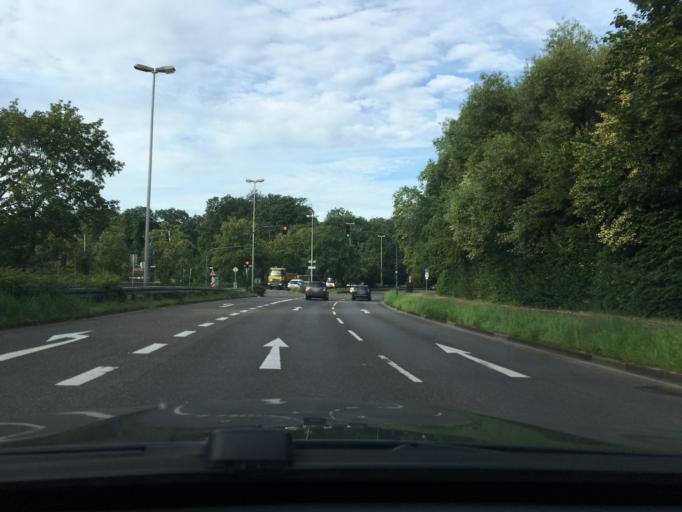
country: DE
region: North Rhine-Westphalia
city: Opladen
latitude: 51.0367
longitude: 7.0319
